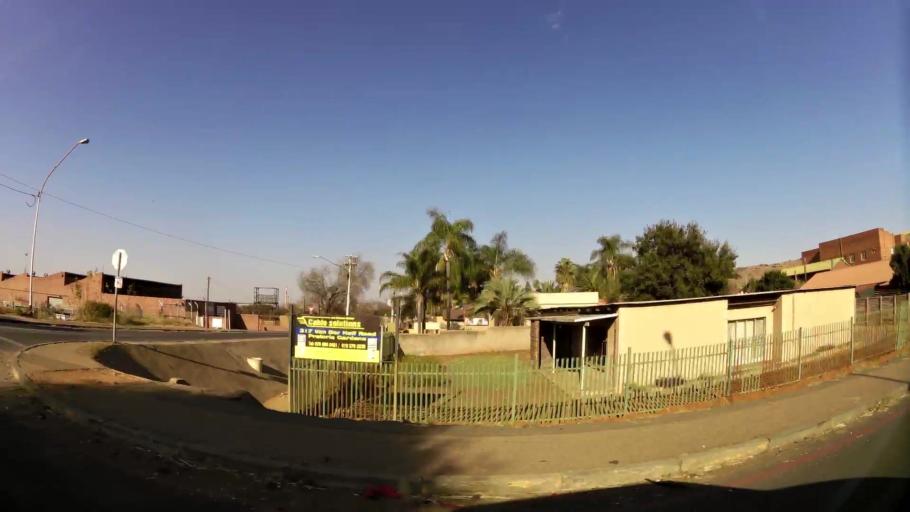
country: ZA
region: Gauteng
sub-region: City of Tshwane Metropolitan Municipality
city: Pretoria
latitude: -25.7187
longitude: 28.1535
